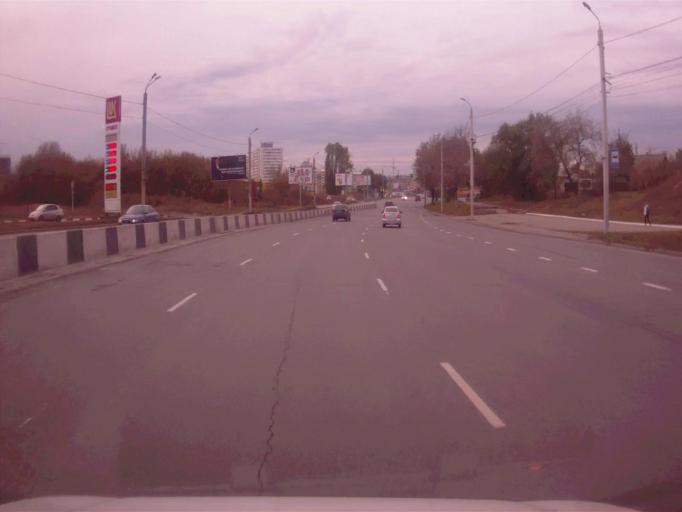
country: RU
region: Chelyabinsk
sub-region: Gorod Chelyabinsk
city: Chelyabinsk
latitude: 55.1744
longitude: 61.3828
